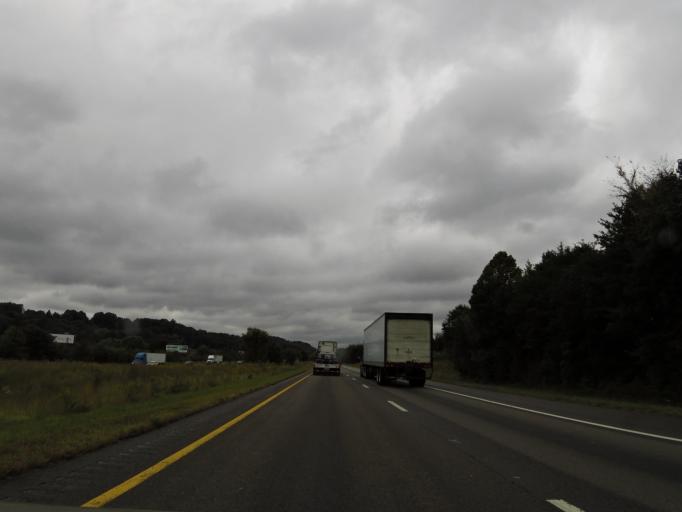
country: US
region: Tennessee
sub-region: Loudon County
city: Loudon
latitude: 35.7734
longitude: -84.3551
